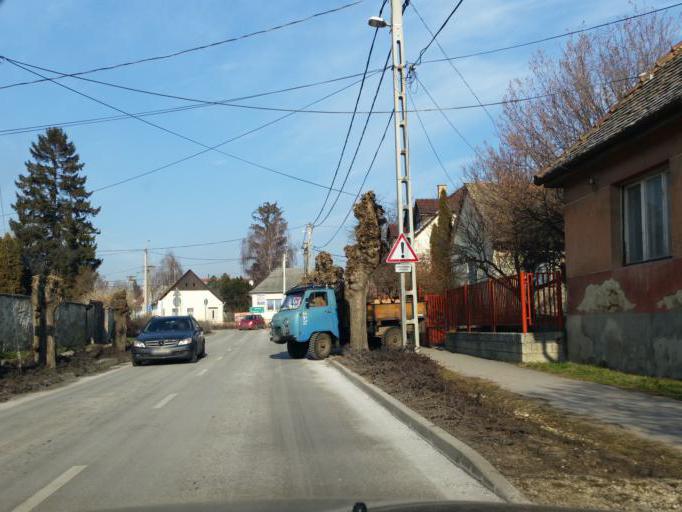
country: HU
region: Pest
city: Paty
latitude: 47.5129
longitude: 18.8250
